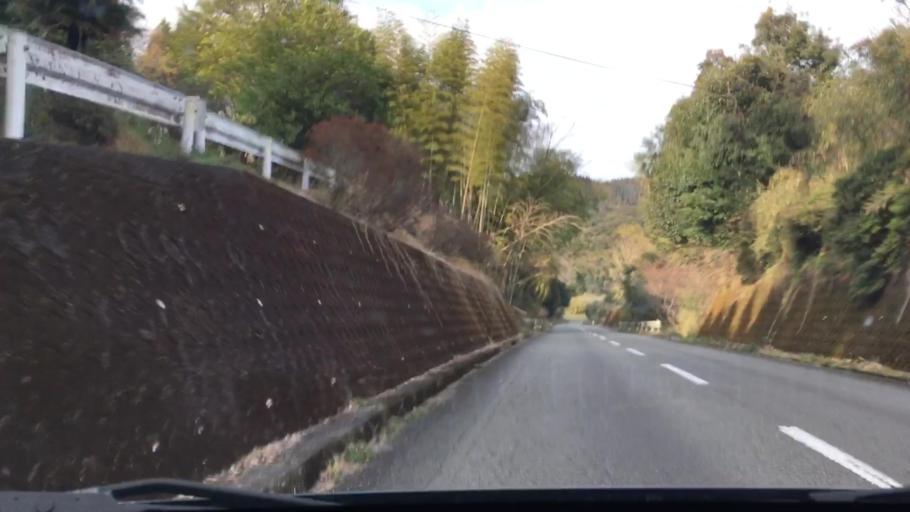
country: JP
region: Miyazaki
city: Nichinan
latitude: 31.5928
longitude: 131.3071
